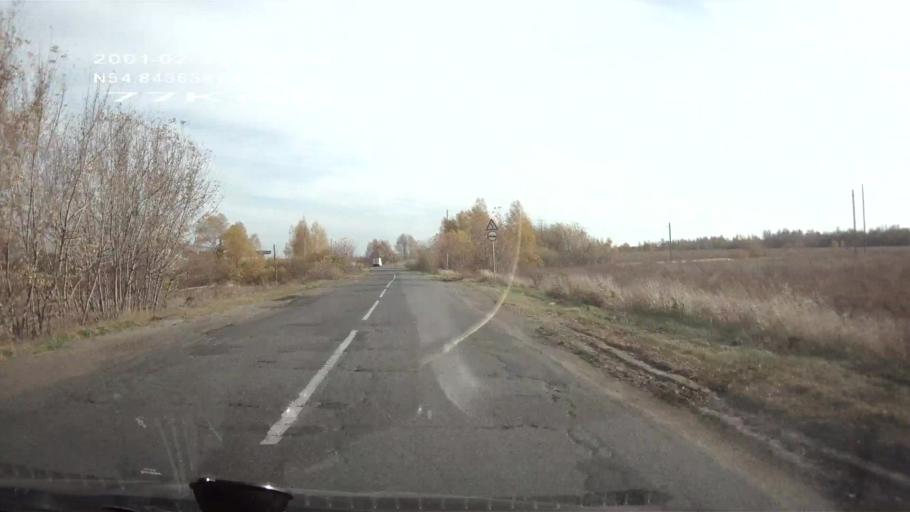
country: RU
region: Chuvashia
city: Alatyr'
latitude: 54.8437
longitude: 46.4713
